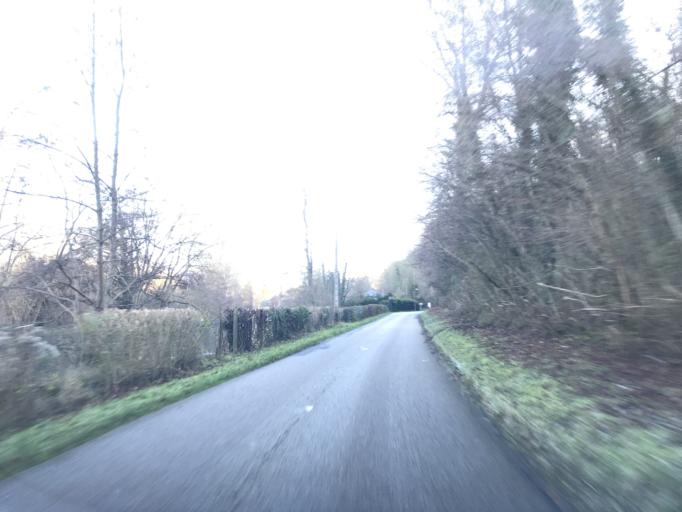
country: FR
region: Haute-Normandie
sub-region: Departement de l'Eure
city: Saint-Aubin-sur-Gaillon
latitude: 49.0909
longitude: 1.2621
